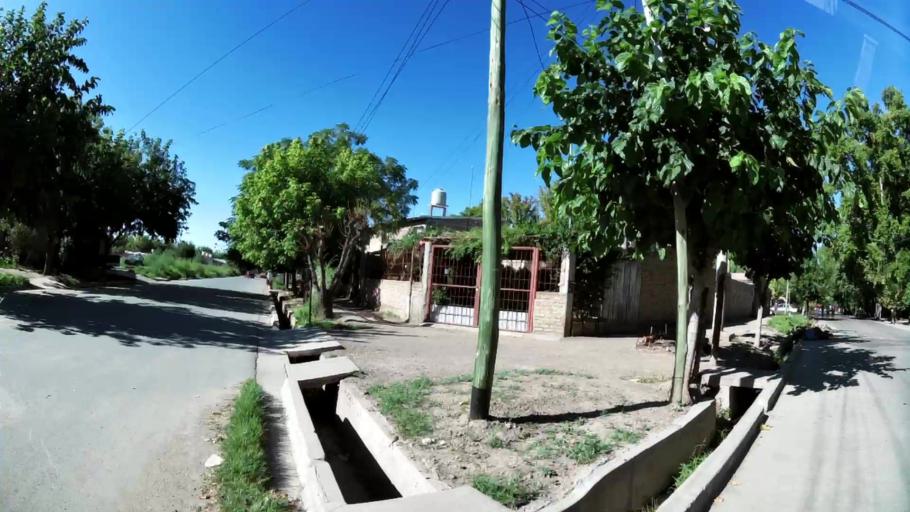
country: AR
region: Mendoza
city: Las Heras
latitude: -32.8408
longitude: -68.8268
